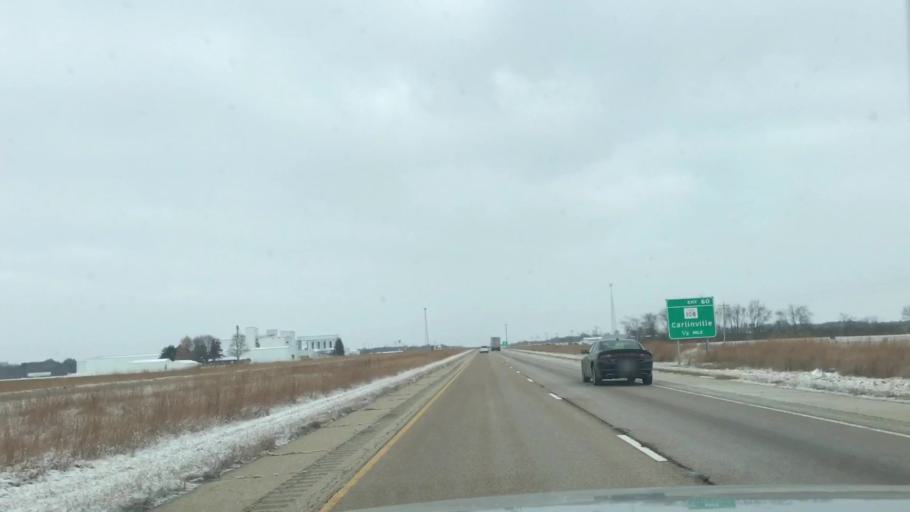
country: US
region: Illinois
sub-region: Montgomery County
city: Raymond
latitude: 39.2659
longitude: -89.6415
